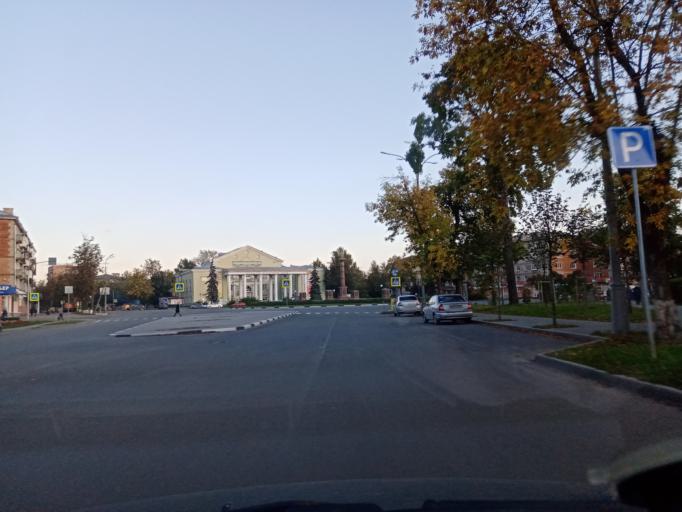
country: RU
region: Pskov
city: Pskov
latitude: 57.8086
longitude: 28.3387
